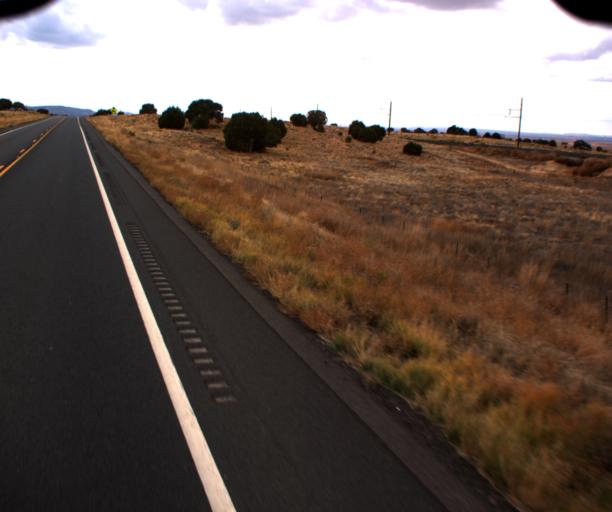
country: US
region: Arizona
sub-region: Navajo County
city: Kayenta
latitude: 36.4992
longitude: -110.6198
